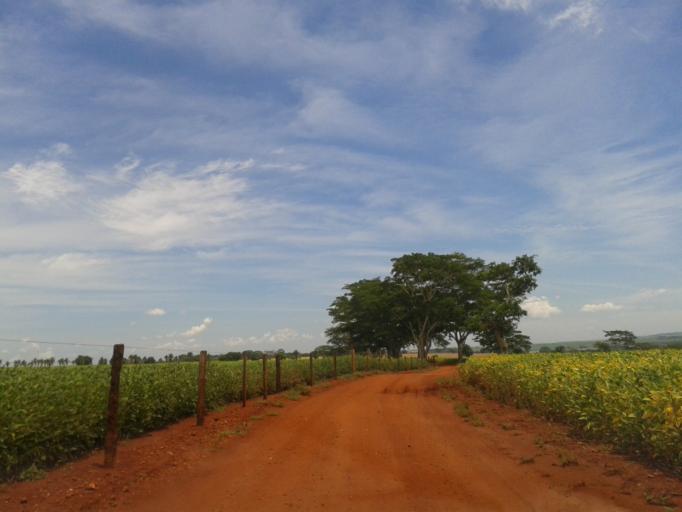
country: BR
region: Minas Gerais
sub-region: Capinopolis
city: Capinopolis
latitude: -18.6546
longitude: -49.7424
